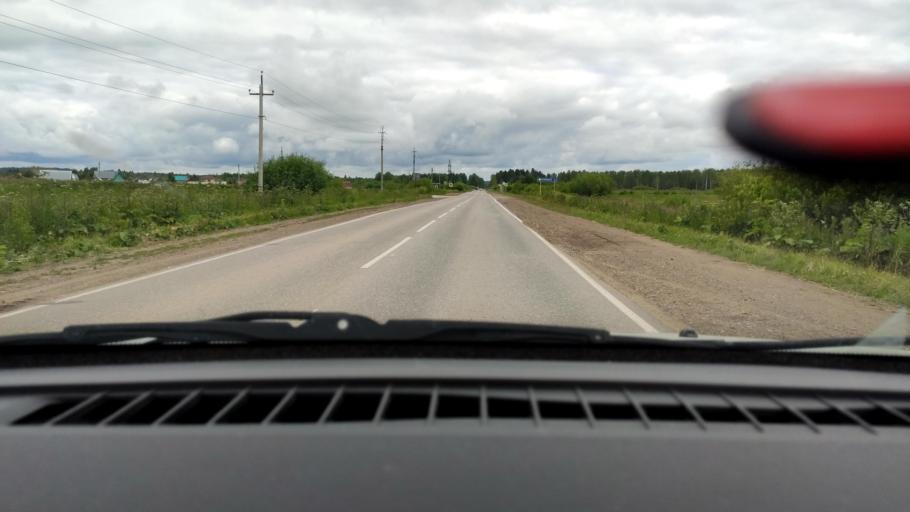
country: RU
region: Perm
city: Ust'-Kachka
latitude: 58.0782
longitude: 55.6178
